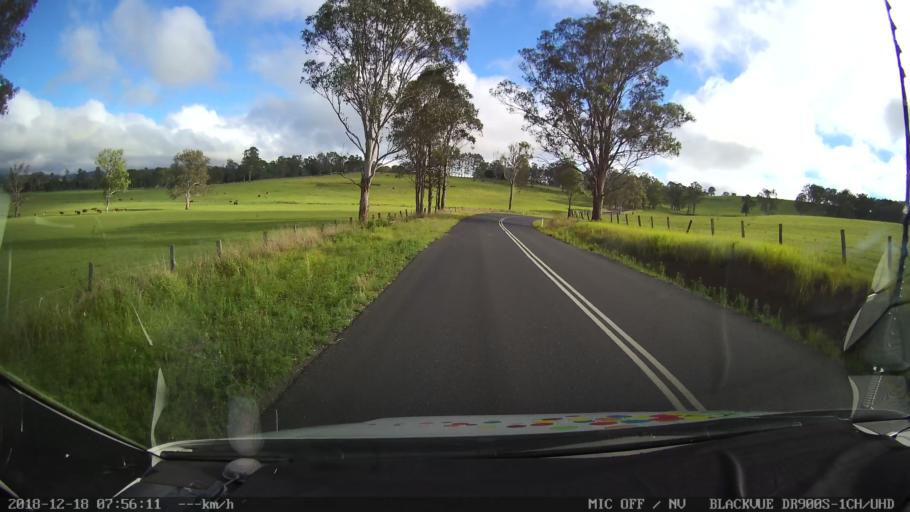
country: AU
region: New South Wales
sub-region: Kyogle
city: Kyogle
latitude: -28.4011
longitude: 152.6044
